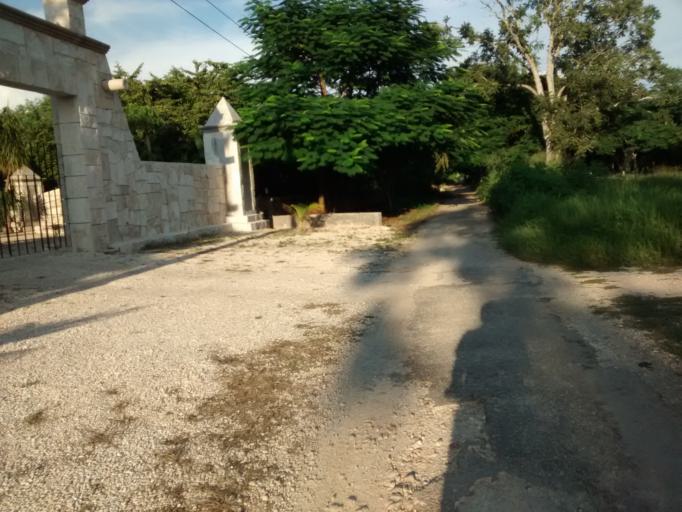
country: MX
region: Yucatan
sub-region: Valladolid
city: Tesoco
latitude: 20.6943
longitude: -88.1679
